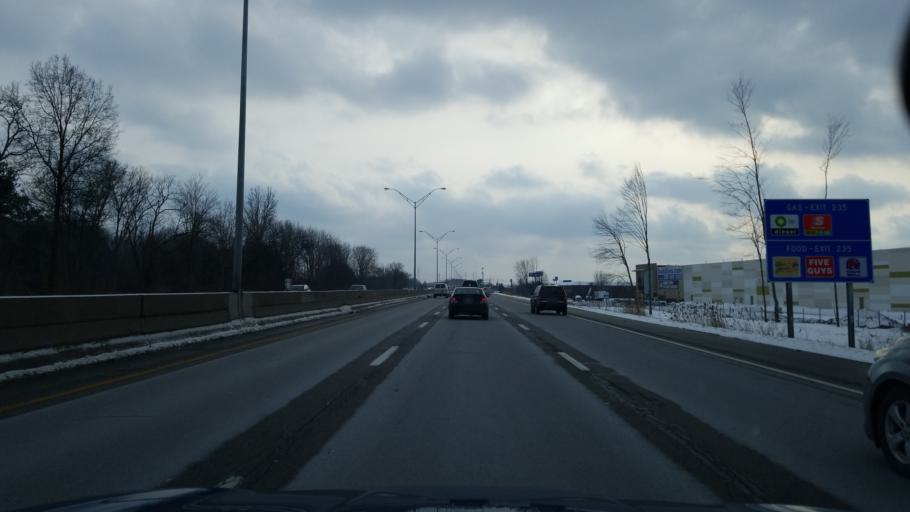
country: US
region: Ohio
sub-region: Cuyahoga County
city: Middleburg Heights
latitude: 41.3798
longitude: -81.8191
